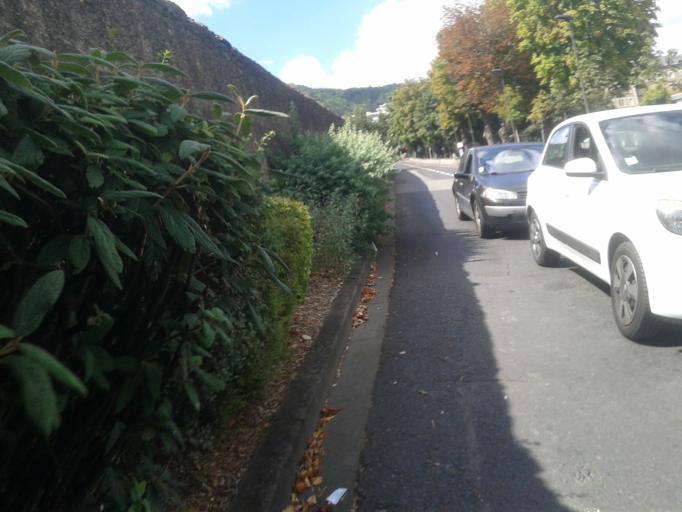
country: FR
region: Auvergne
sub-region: Departement du Puy-de-Dome
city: Chamalieres
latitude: 45.7761
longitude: 3.0623
